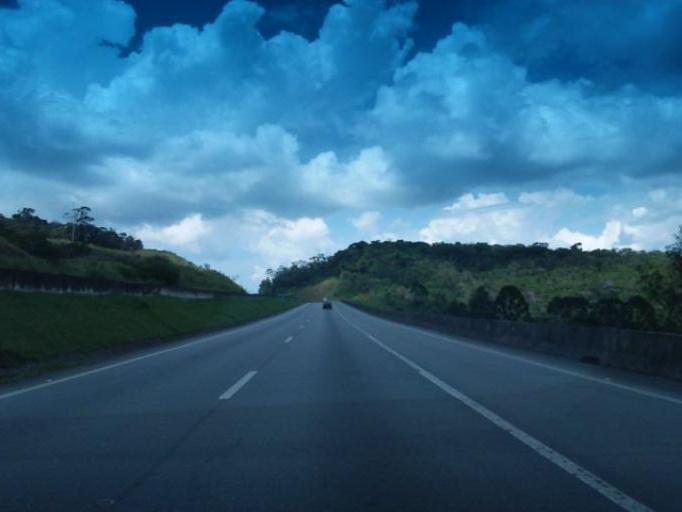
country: BR
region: Sao Paulo
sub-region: Juquitiba
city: Juquitiba
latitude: -24.0096
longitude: -47.1622
